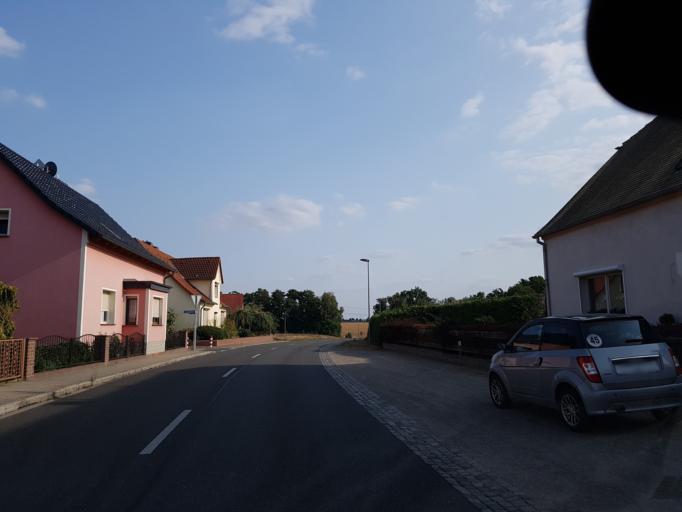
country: DE
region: Saxony
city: Dommitzsch
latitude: 51.6689
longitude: 12.8409
